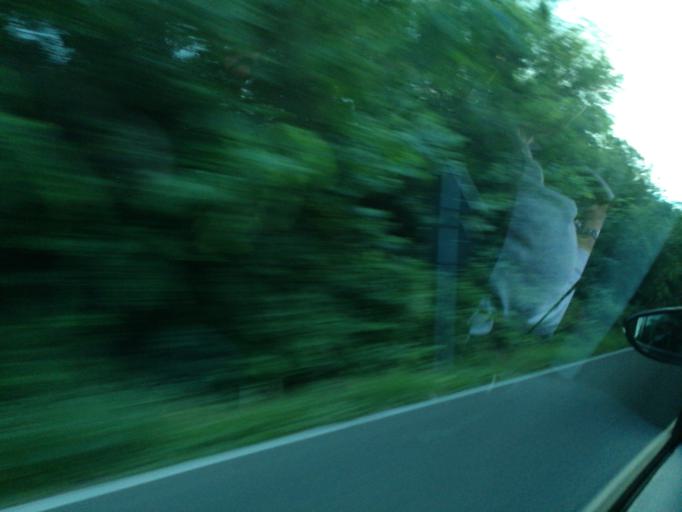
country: RO
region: Constanta
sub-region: Comuna Douazeci si Trei August
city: Douazeci si Trei August
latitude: 43.8588
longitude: 28.5852
